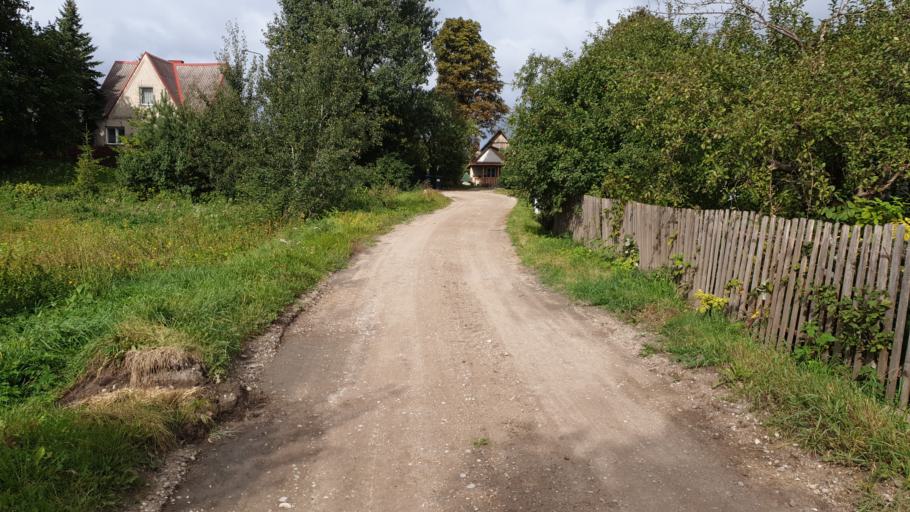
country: LT
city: Moletai
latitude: 55.2341
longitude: 25.4182
